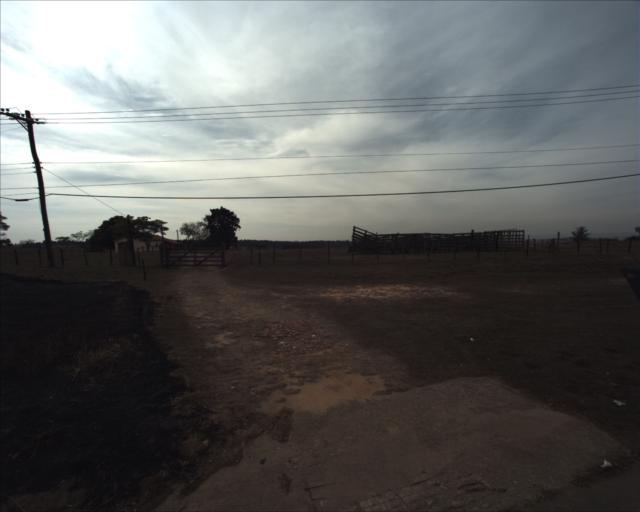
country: BR
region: Sao Paulo
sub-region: Sorocaba
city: Sorocaba
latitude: -23.3982
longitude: -47.5160
